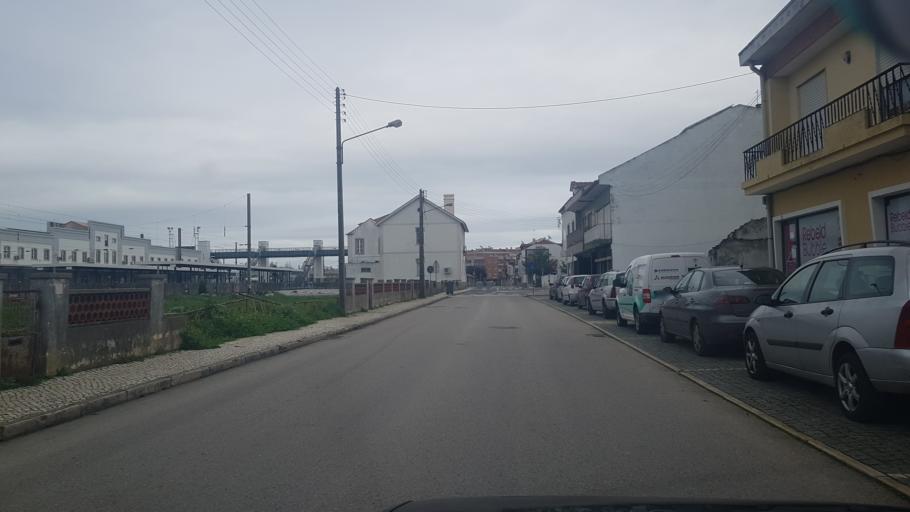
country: PT
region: Santarem
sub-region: Entroncamento
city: Entroncamento
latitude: 39.4604
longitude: -8.4740
